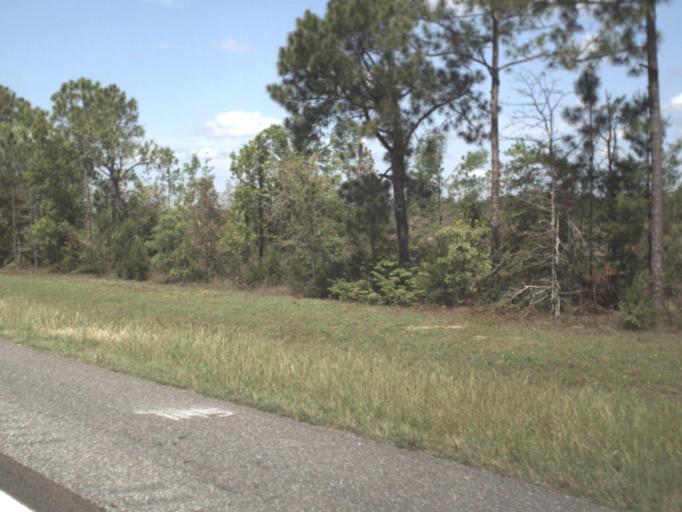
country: US
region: Florida
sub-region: Santa Rosa County
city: East Milton
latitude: 30.6754
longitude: -86.8293
